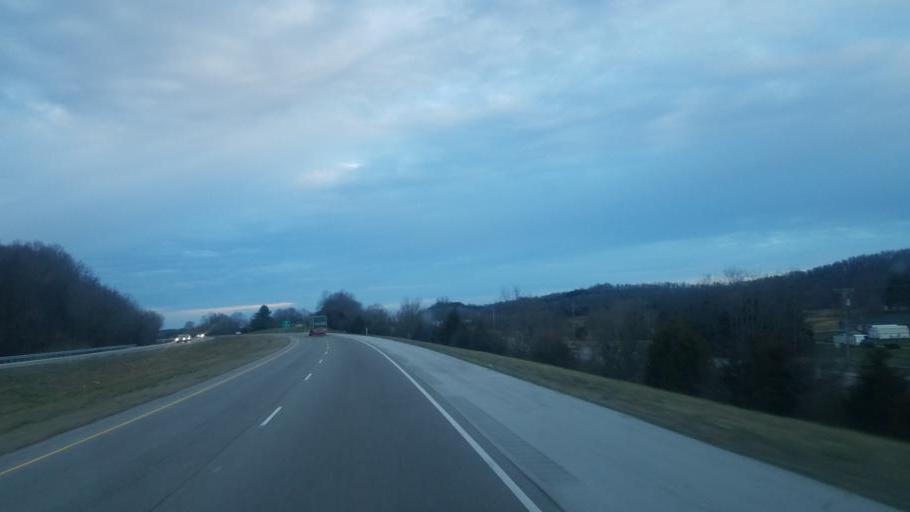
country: US
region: Tennessee
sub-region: White County
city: Sparta
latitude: 35.9764
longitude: -85.4905
